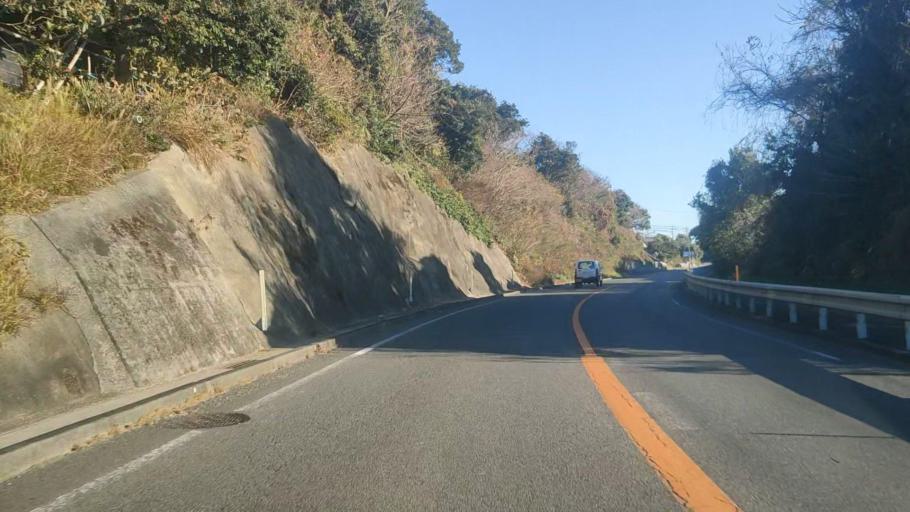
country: JP
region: Miyazaki
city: Nobeoka
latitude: 32.3648
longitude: 131.6237
